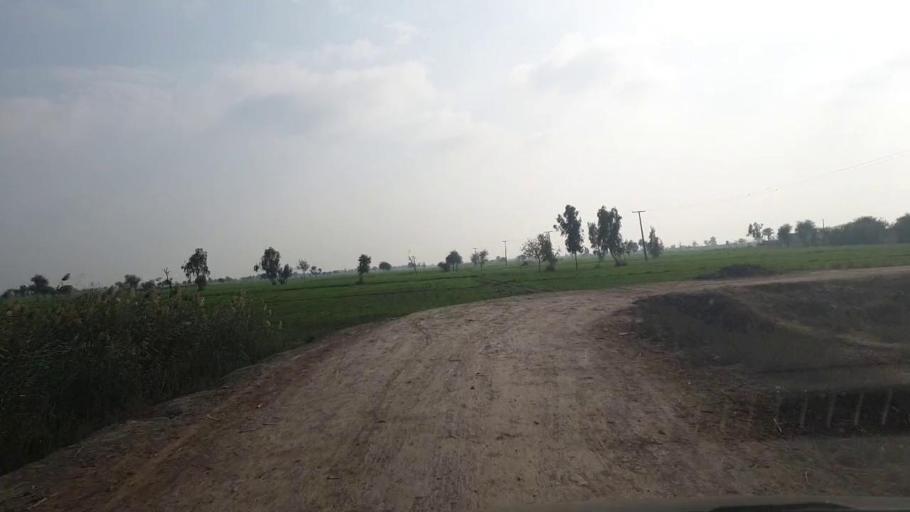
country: PK
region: Sindh
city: Shahdadpur
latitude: 25.8721
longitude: 68.6647
